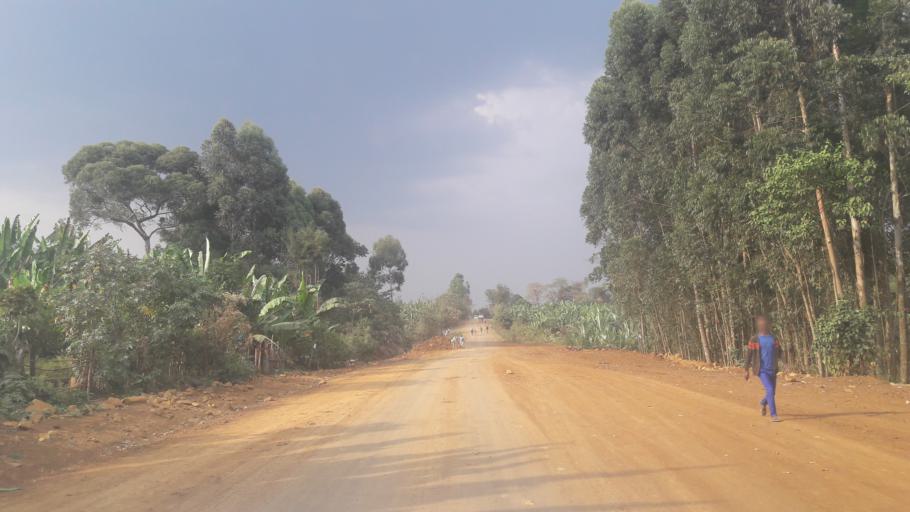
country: ET
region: Oromiya
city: Gore
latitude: 7.7250
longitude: 35.4832
